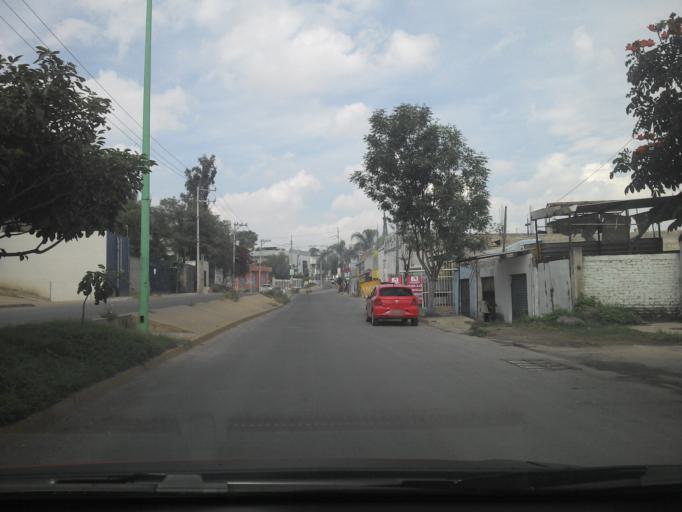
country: MX
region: Jalisco
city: Las Pintas de Arriba
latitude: 20.5907
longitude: -103.3495
